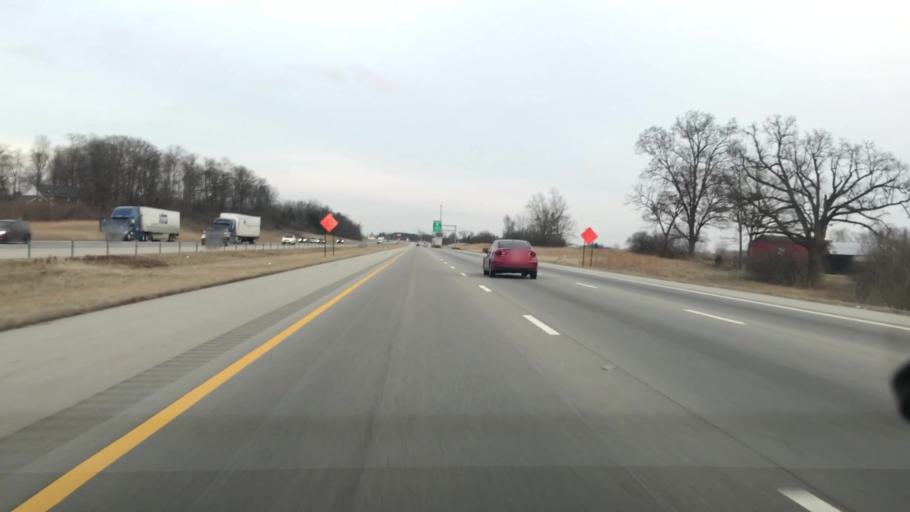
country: US
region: Ohio
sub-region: Clark County
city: Enon
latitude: 39.8925
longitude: -83.8990
